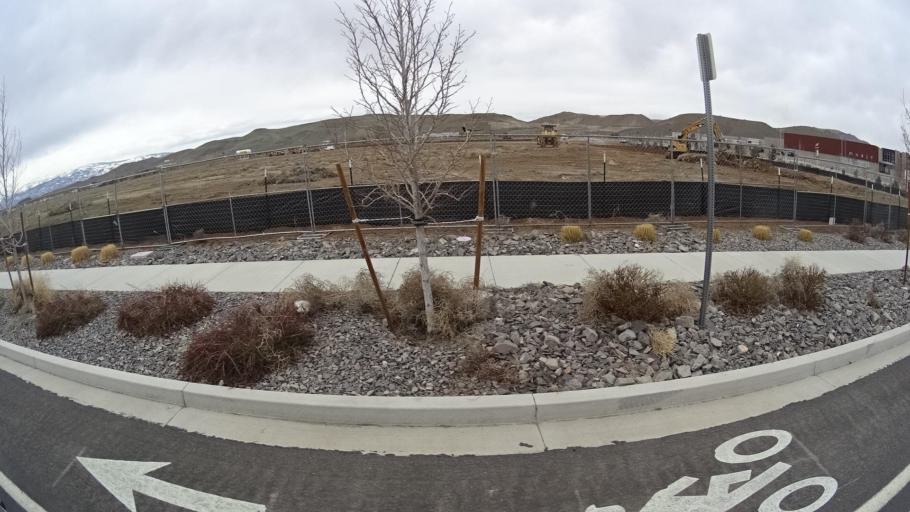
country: US
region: Nevada
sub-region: Washoe County
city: Spanish Springs
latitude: 39.6081
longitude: -119.7203
